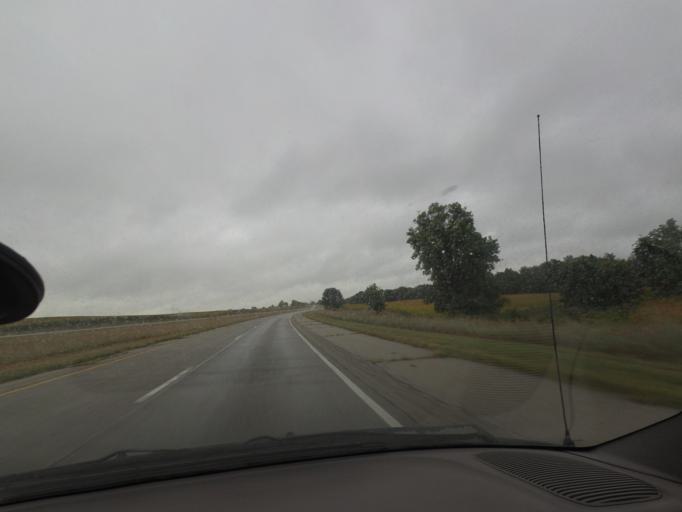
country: US
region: Illinois
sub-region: Pike County
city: Barry
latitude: 39.7399
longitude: -91.1351
